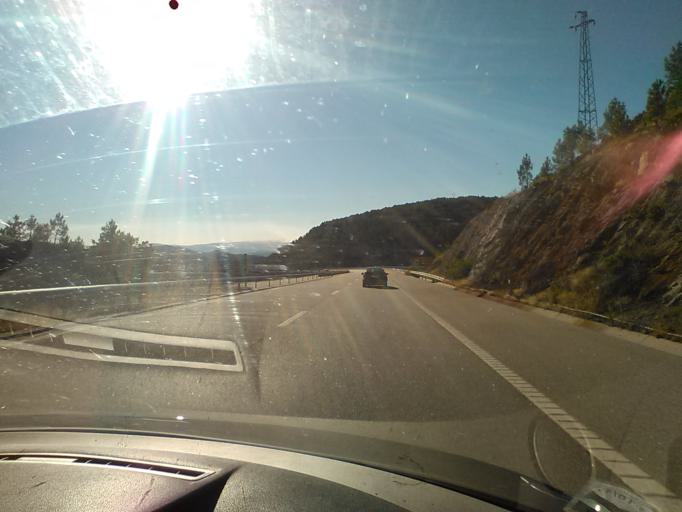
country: PT
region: Vila Real
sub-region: Ribeira de Pena
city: Ribeira de Pena
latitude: 41.5015
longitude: -7.7642
